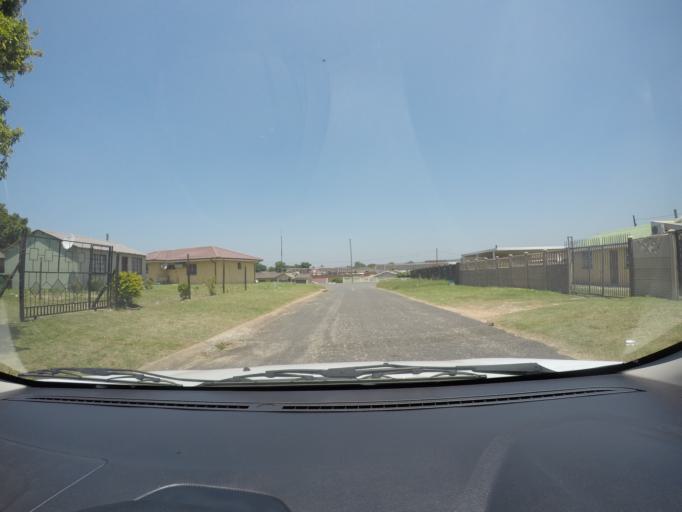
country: ZA
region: KwaZulu-Natal
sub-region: uThungulu District Municipality
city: eSikhawini
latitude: -28.8748
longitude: 31.9074
